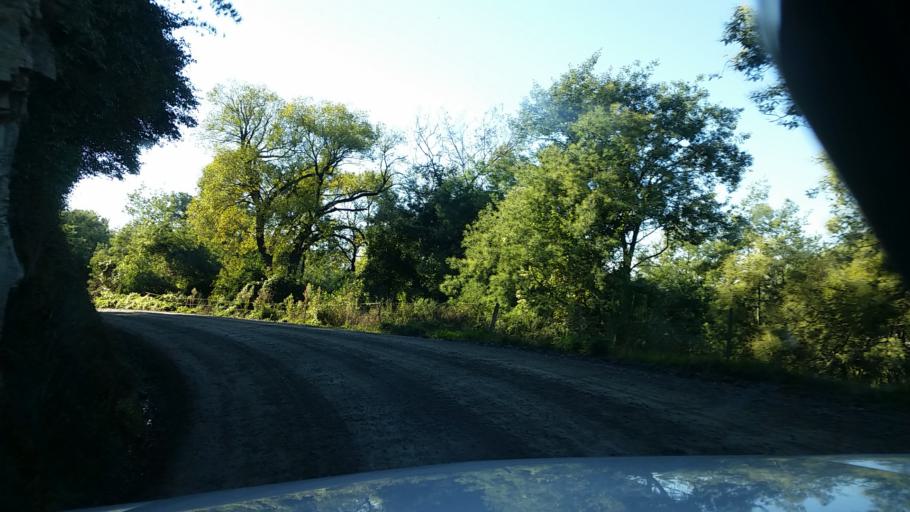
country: NZ
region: Marlborough
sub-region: Marlborough District
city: Blenheim
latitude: -41.4462
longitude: 173.8927
